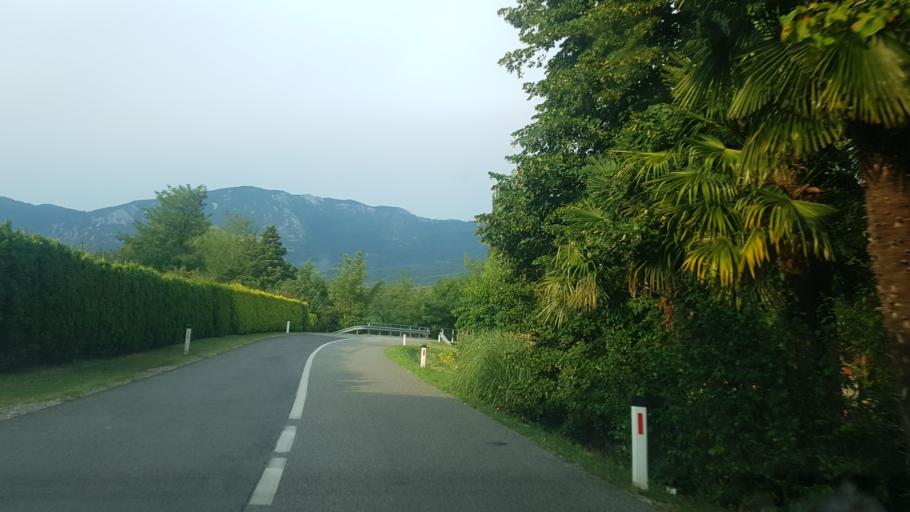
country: SI
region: Nova Gorica
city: Sempas
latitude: 45.8906
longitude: 13.7688
